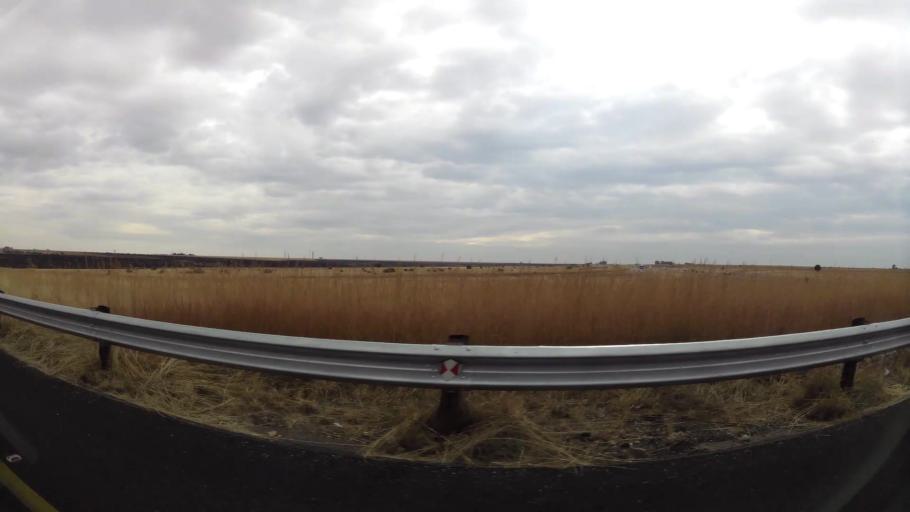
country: ZA
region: Orange Free State
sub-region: Fezile Dabi District Municipality
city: Kroonstad
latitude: -27.6242
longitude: 27.2529
